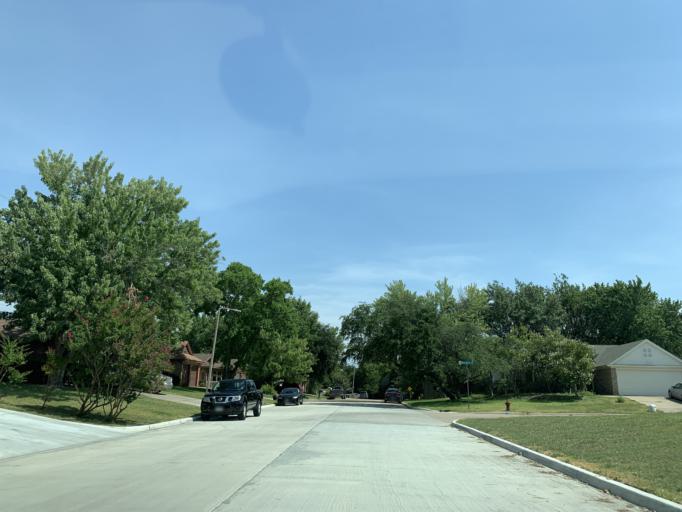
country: US
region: Texas
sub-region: Dallas County
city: Grand Prairie
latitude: 32.6672
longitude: -97.0355
